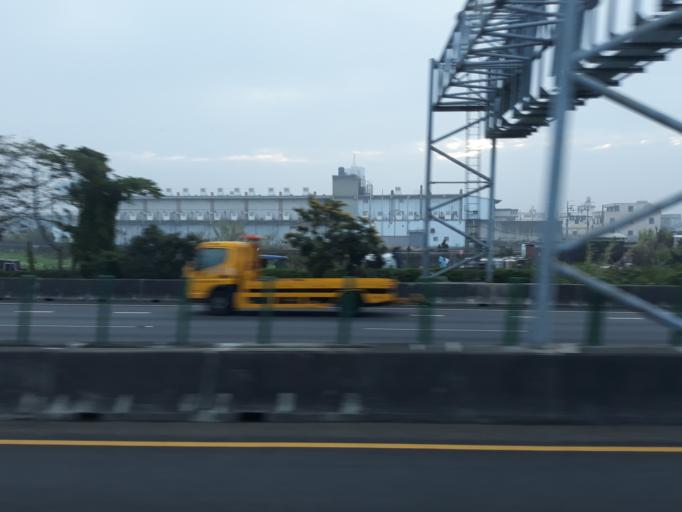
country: TW
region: Taiwan
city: Fengyuan
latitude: 24.3036
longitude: 120.6980
